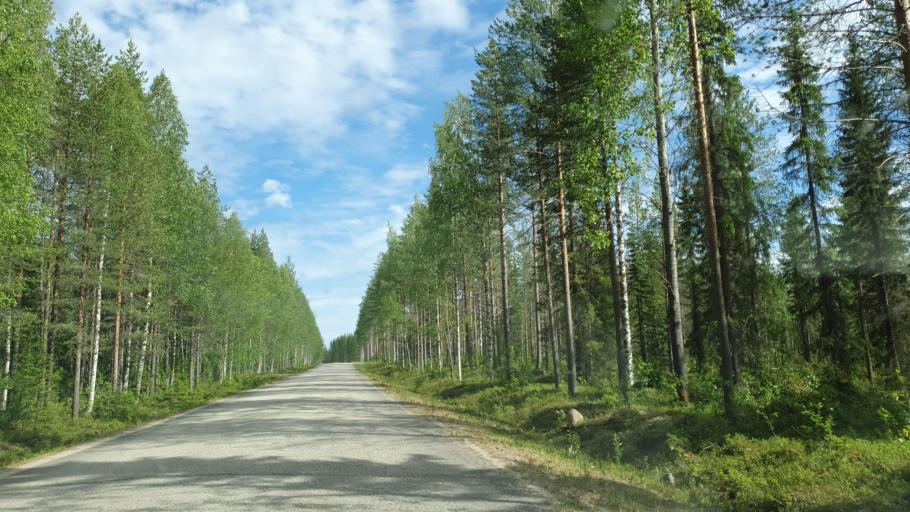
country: FI
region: Kainuu
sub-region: Kehys-Kainuu
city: Kuhmo
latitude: 64.5178
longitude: 29.3871
